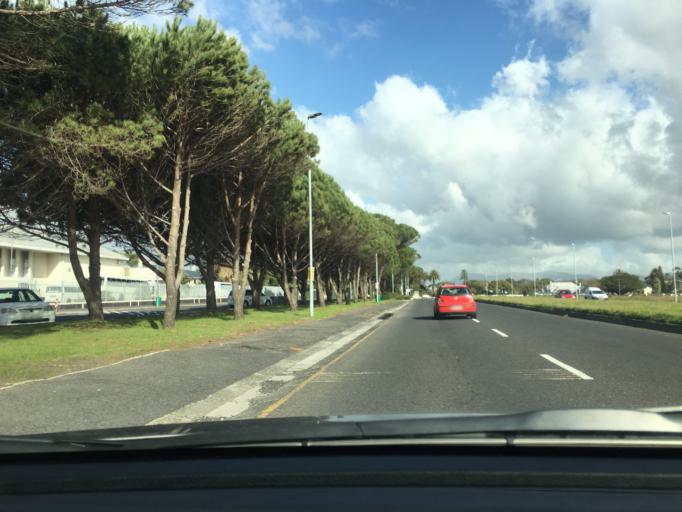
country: ZA
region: Western Cape
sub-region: City of Cape Town
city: Rondebosch
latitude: -33.9565
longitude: 18.4857
